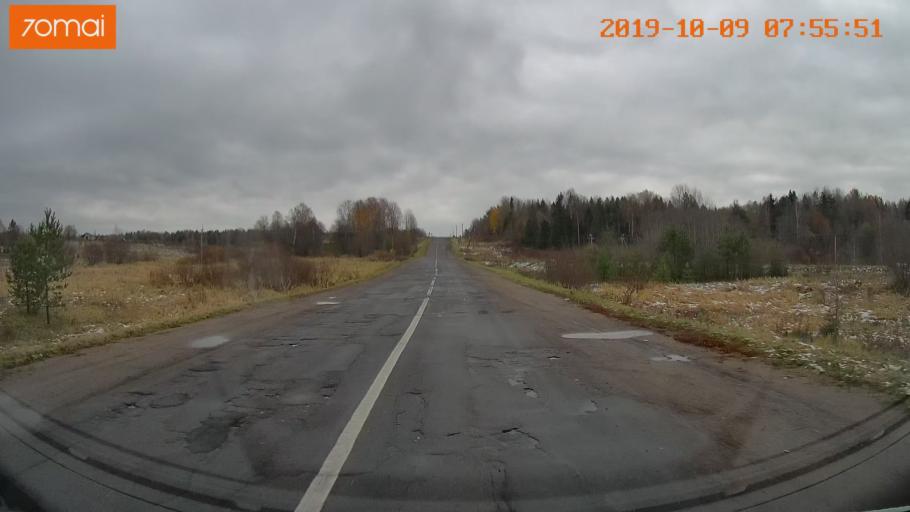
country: RU
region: Jaroslavl
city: Kukoboy
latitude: 58.6990
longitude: 39.9268
